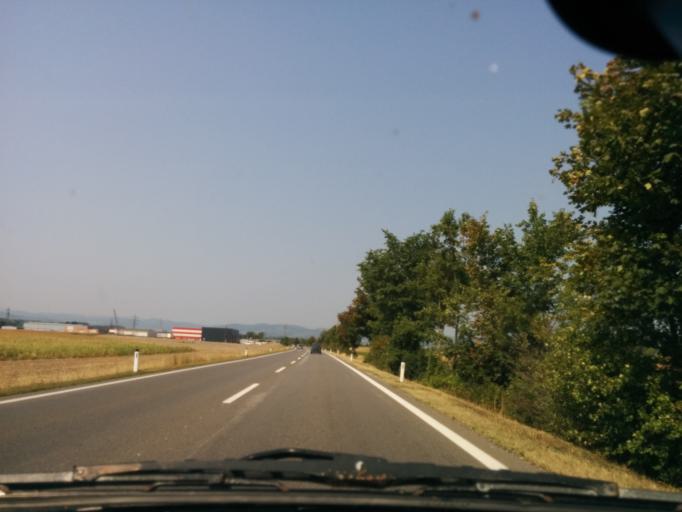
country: AT
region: Lower Austria
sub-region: Politischer Bezirk Krems
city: Gedersdorf
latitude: 48.4127
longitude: 15.7020
